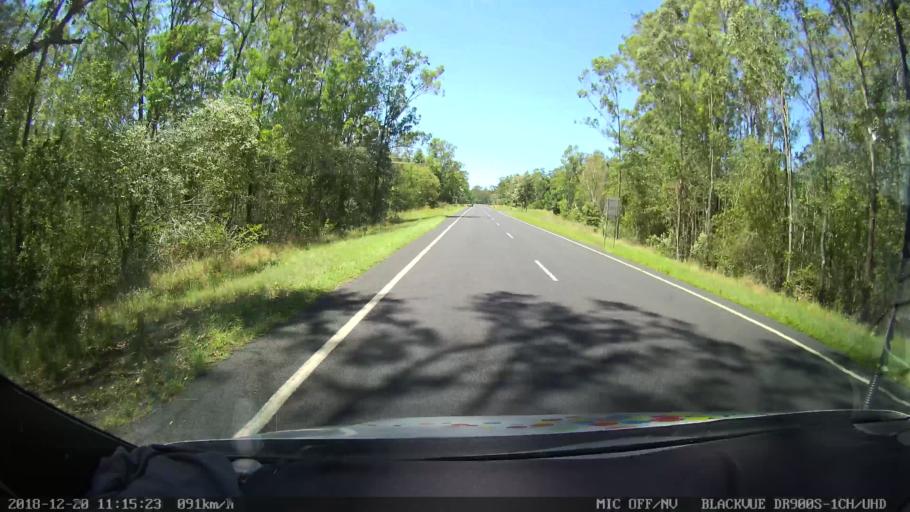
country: AU
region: New South Wales
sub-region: Richmond Valley
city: Casino
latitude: -29.0126
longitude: 153.0083
